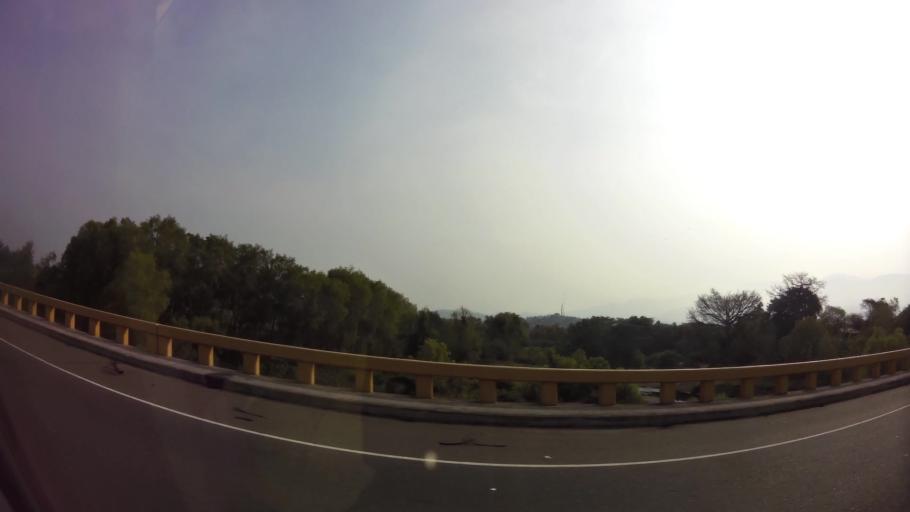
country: HN
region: Comayagua
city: Comayagua
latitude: 14.4331
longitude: -87.6495
